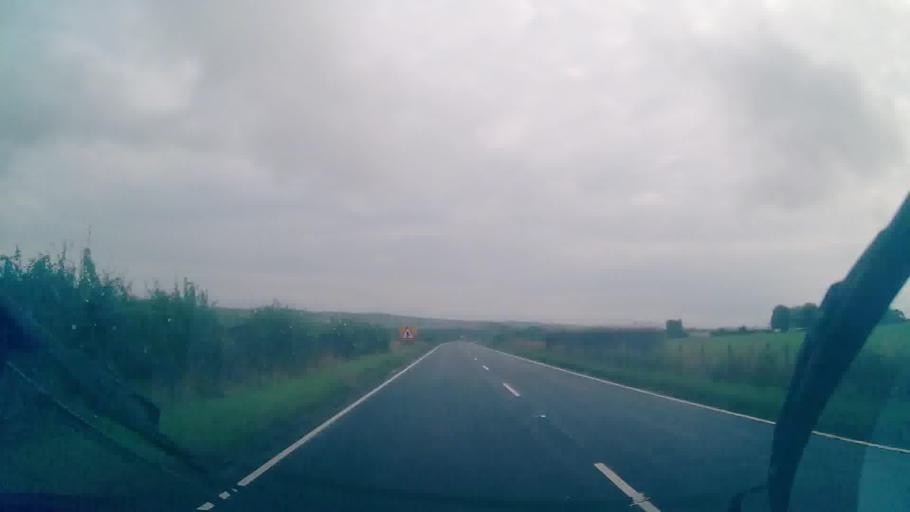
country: GB
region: Scotland
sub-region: Dumfries and Galloway
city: Locharbriggs
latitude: 55.0688
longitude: -3.5427
